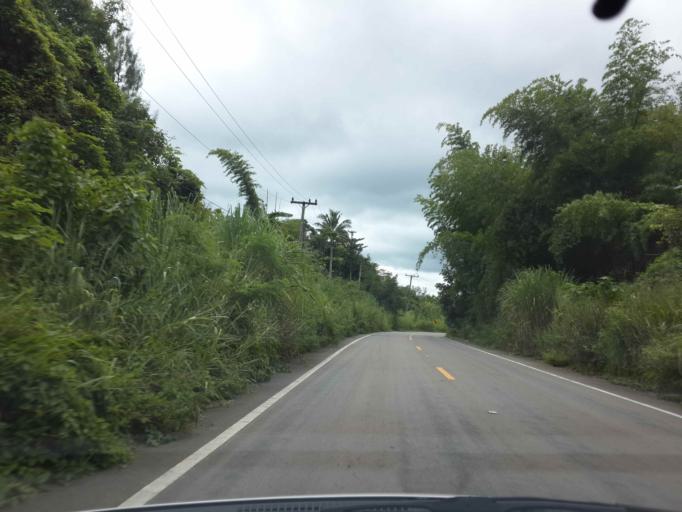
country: TH
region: Ratchaburi
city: Suan Phueng
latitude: 13.6731
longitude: 99.2029
